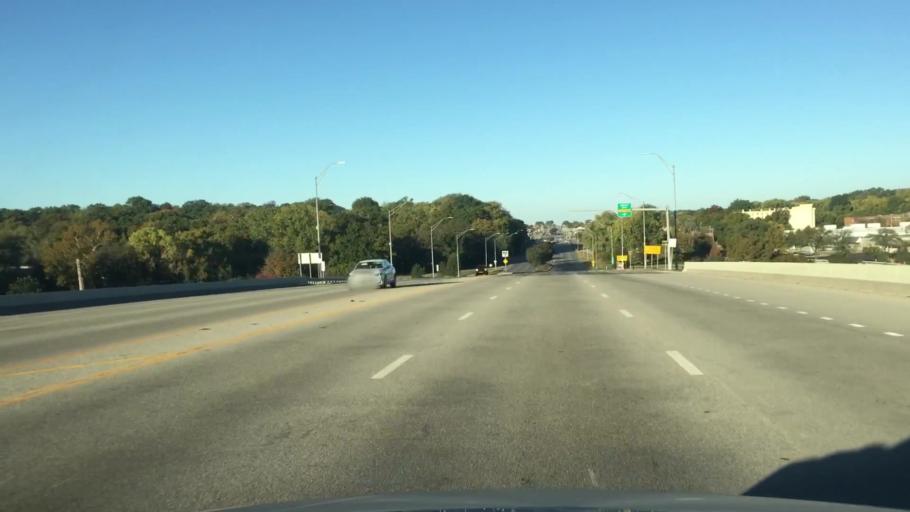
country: US
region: Kansas
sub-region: Johnson County
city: Merriam
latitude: 39.0149
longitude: -94.6961
